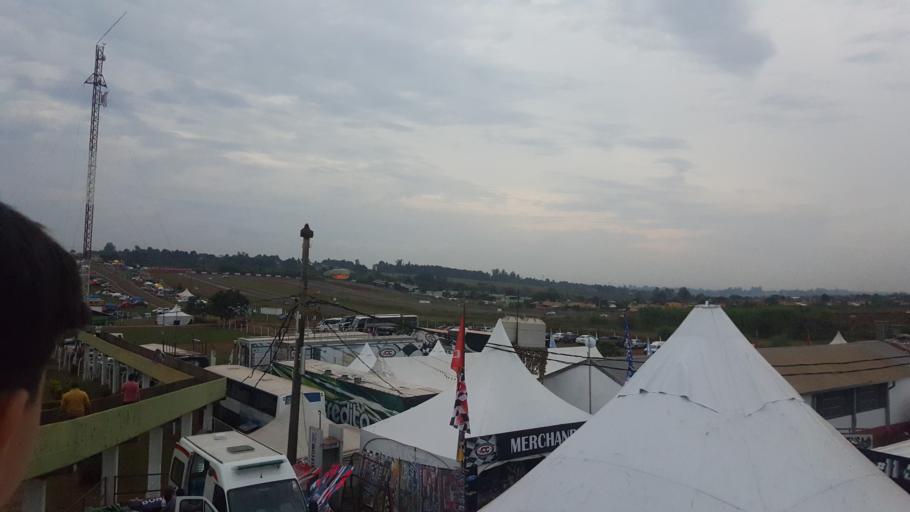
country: AR
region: Entre Rios
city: Concepcion del Uruguay
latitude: -32.4549
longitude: -58.3182
